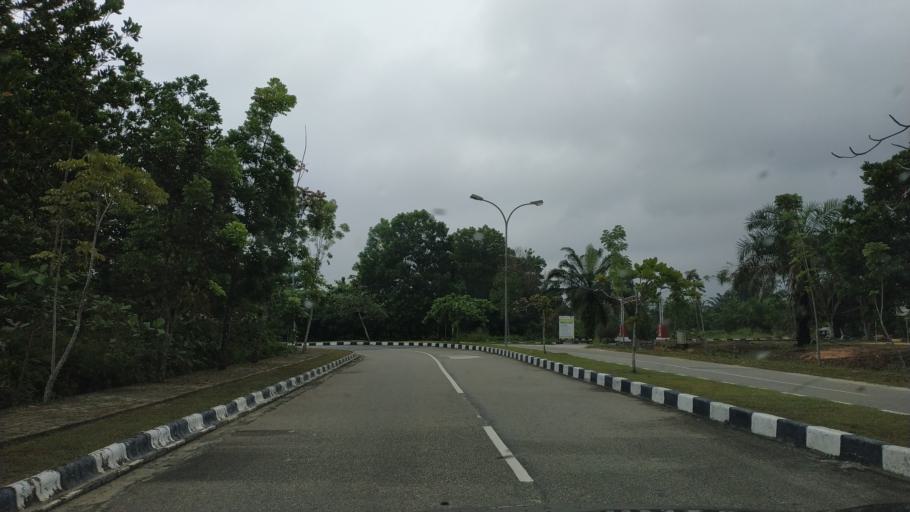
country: ID
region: Riau
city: Pangkalanbunut
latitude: 0.3814
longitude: 101.8238
